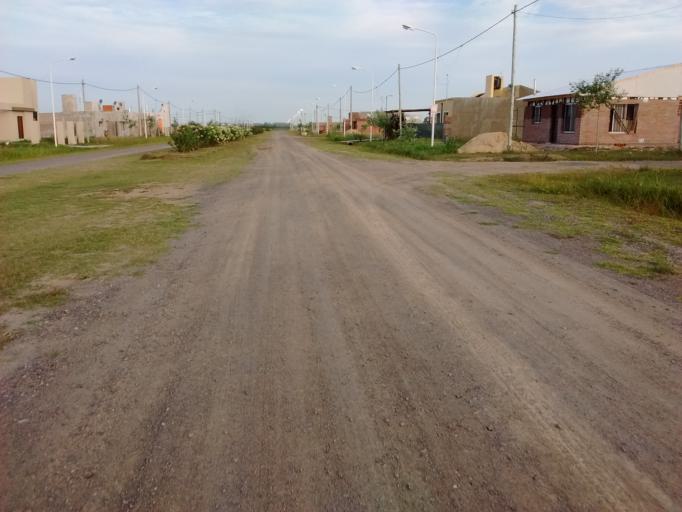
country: AR
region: Santa Fe
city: Roldan
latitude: -32.9381
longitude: -60.8793
